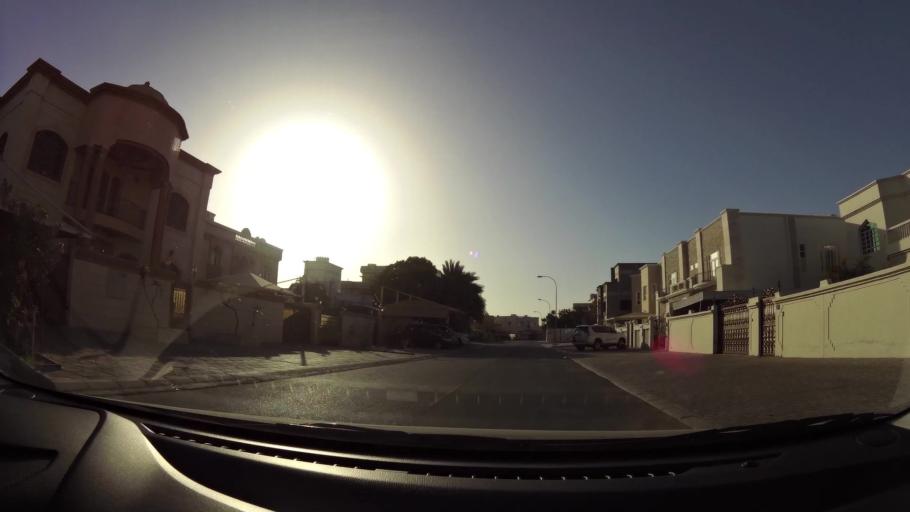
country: OM
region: Muhafazat Masqat
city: As Sib al Jadidah
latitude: 23.6095
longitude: 58.2181
